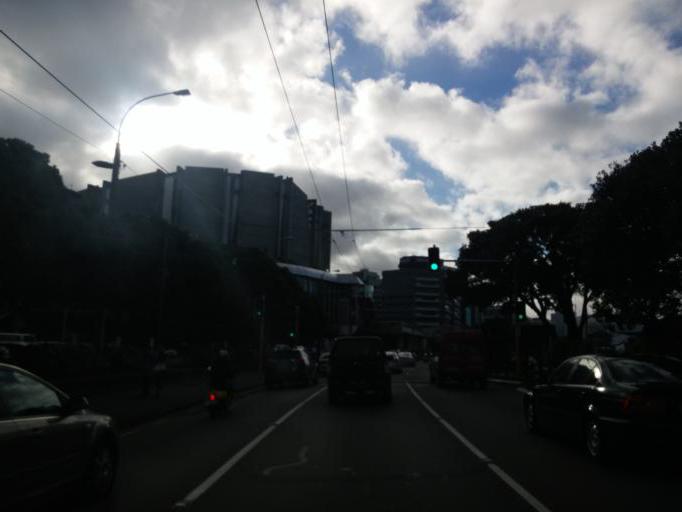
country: NZ
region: Wellington
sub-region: Wellington City
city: Wellington
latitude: -41.2902
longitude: 174.7788
